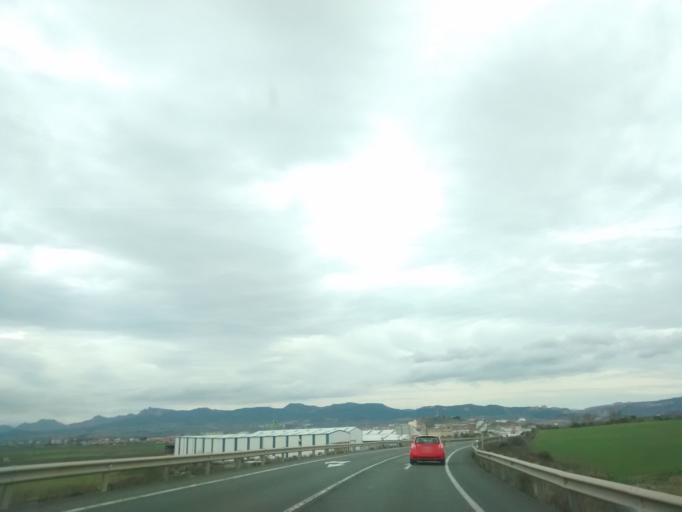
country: ES
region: La Rioja
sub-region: Provincia de La Rioja
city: Ollauri
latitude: 42.5506
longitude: -2.8333
